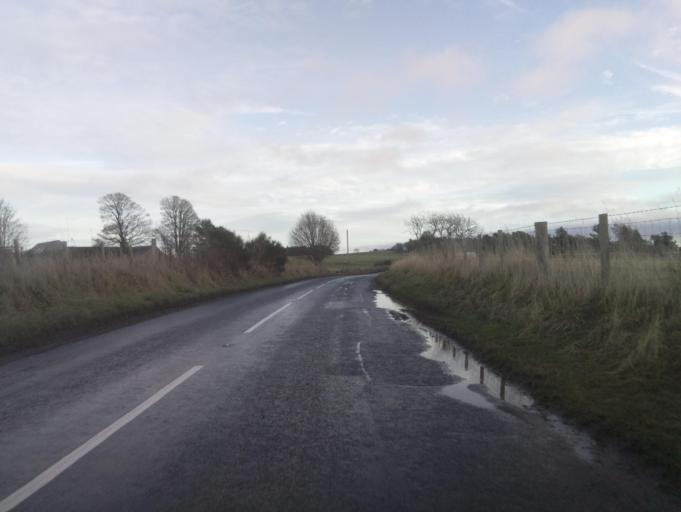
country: GB
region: Scotland
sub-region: Angus
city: Letham
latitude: 56.5847
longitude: -2.8241
